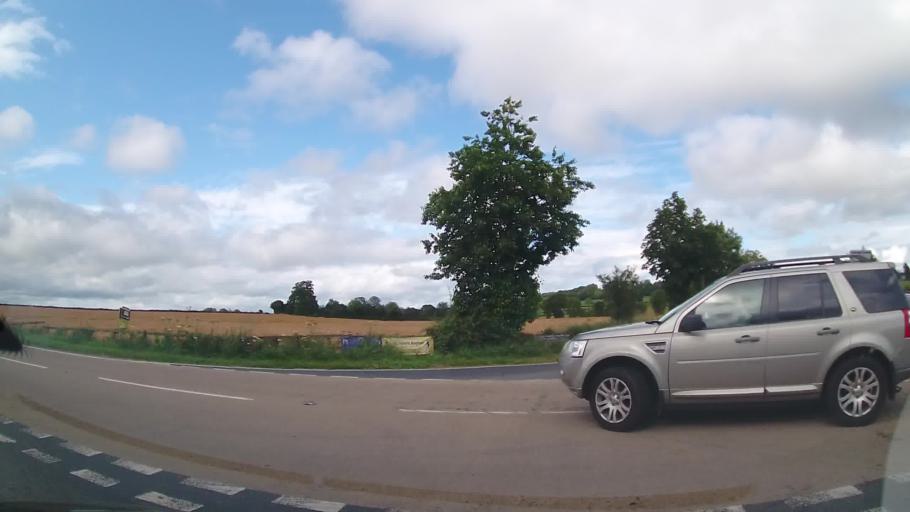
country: GB
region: England
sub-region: Shropshire
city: Great Ness
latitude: 52.7986
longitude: -2.9503
